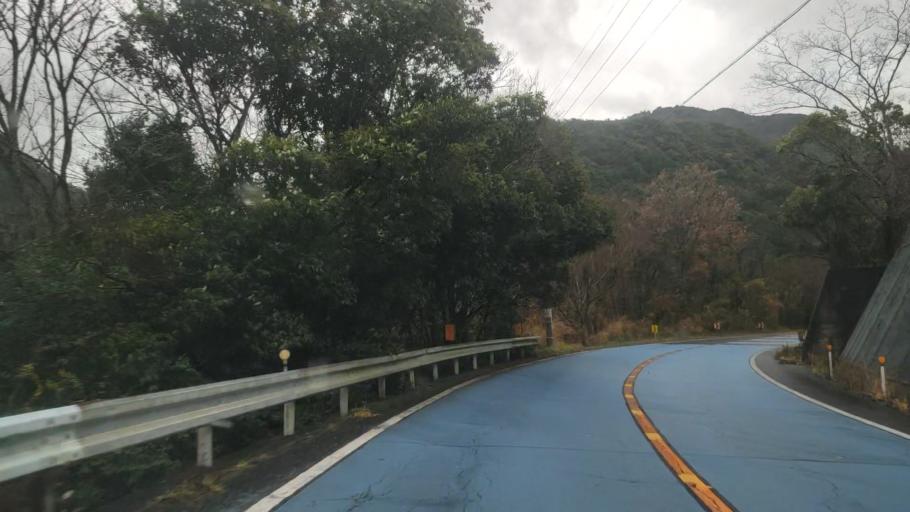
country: JP
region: Tokushima
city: Kamojimacho-jogejima
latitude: 34.1871
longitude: 134.3369
